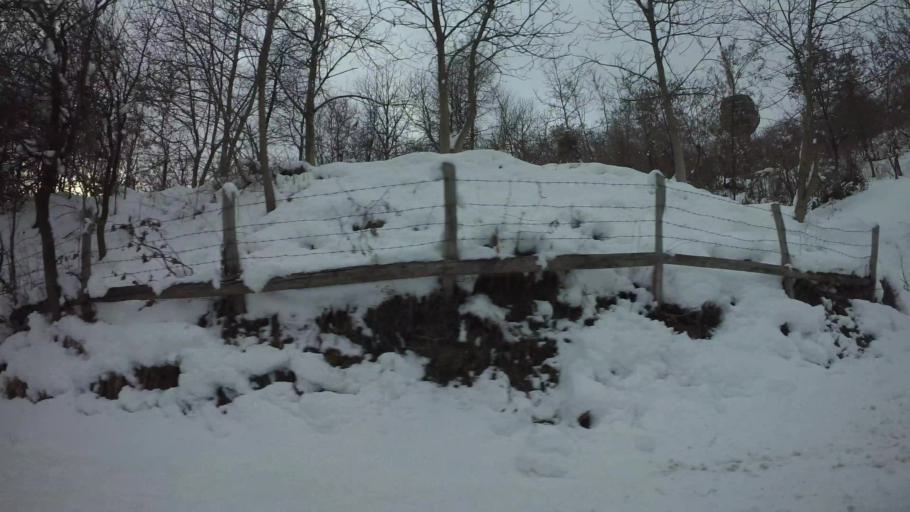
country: BA
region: Federation of Bosnia and Herzegovina
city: Kobilja Glava
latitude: 43.8713
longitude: 18.3885
